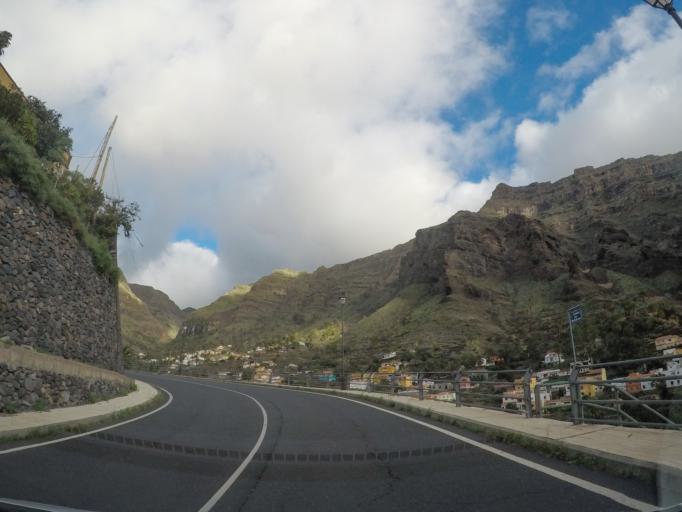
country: ES
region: Canary Islands
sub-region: Provincia de Santa Cruz de Tenerife
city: Vallehermosa
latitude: 28.1125
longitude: -17.3157
